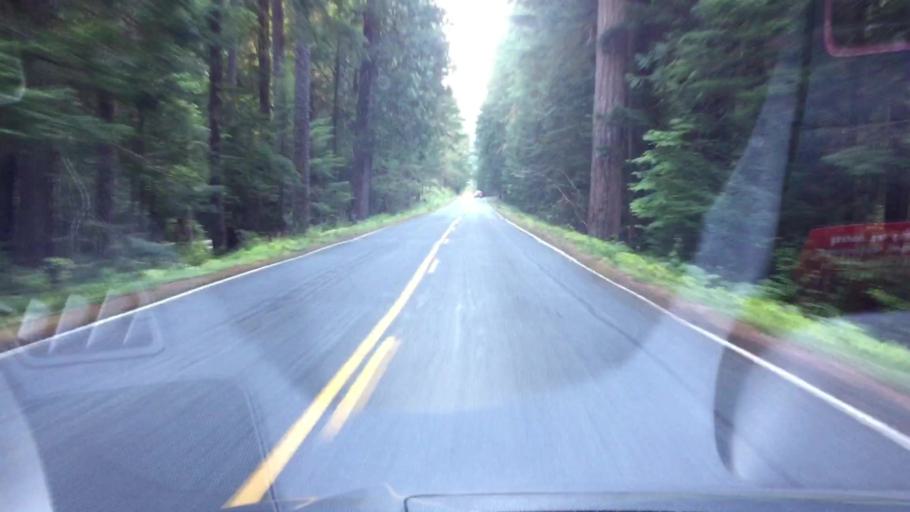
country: US
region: Washington
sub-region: Pierce County
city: Buckley
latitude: 46.7259
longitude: -121.5737
